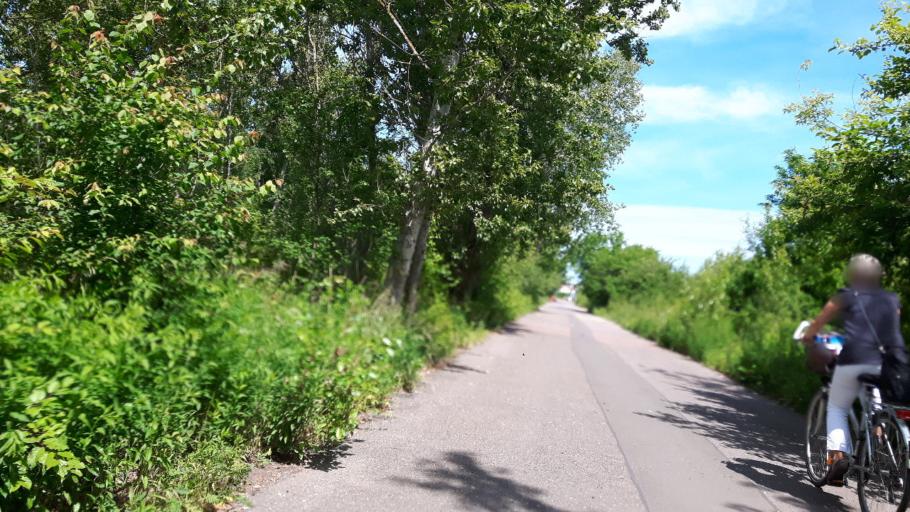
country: DE
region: Saxony
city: Markranstadt
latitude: 51.3138
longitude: 12.2603
